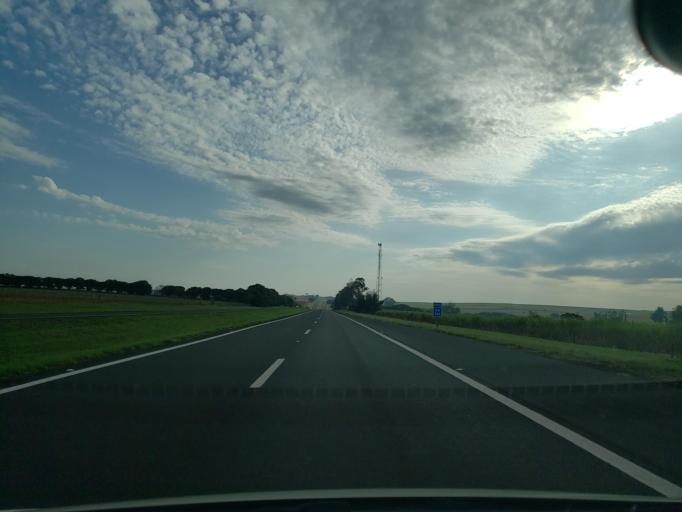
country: BR
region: Sao Paulo
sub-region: Valparaiso
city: Valparaiso
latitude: -21.2068
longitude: -50.7607
